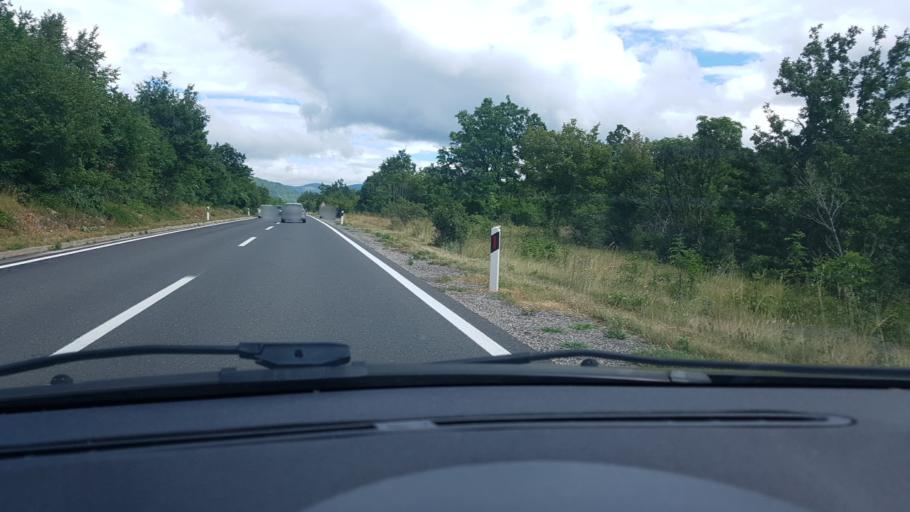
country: HR
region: Zadarska
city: Gracac
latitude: 44.4584
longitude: 15.8162
